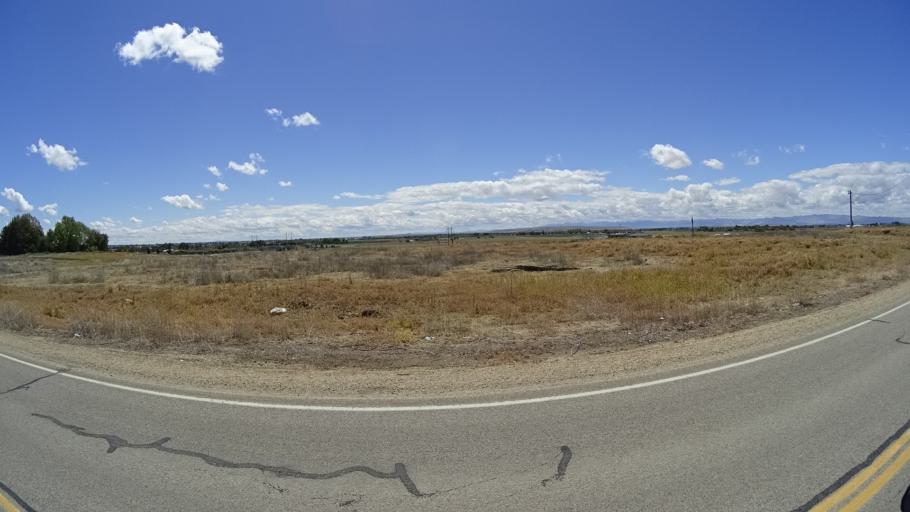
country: US
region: Idaho
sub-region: Ada County
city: Kuna
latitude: 43.5466
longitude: -116.4062
